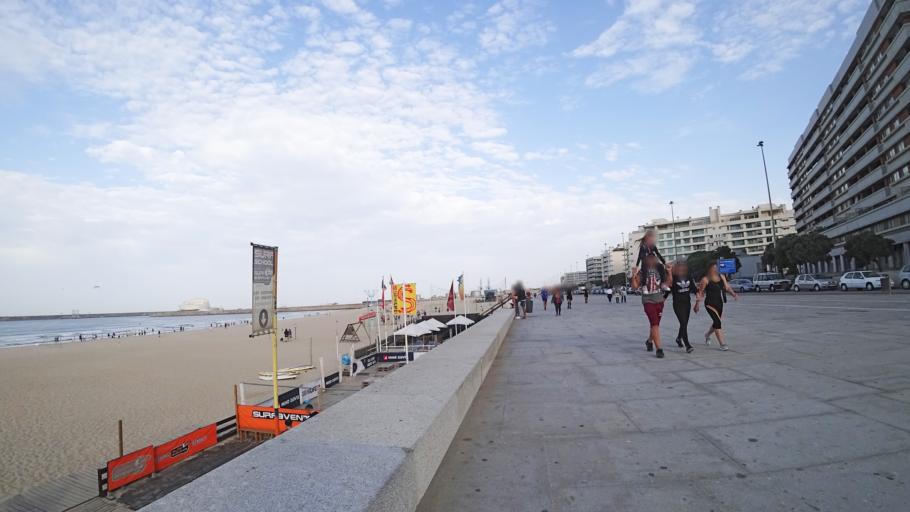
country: PT
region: Porto
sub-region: Matosinhos
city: Matosinhos
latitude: 41.1752
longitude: -8.6905
